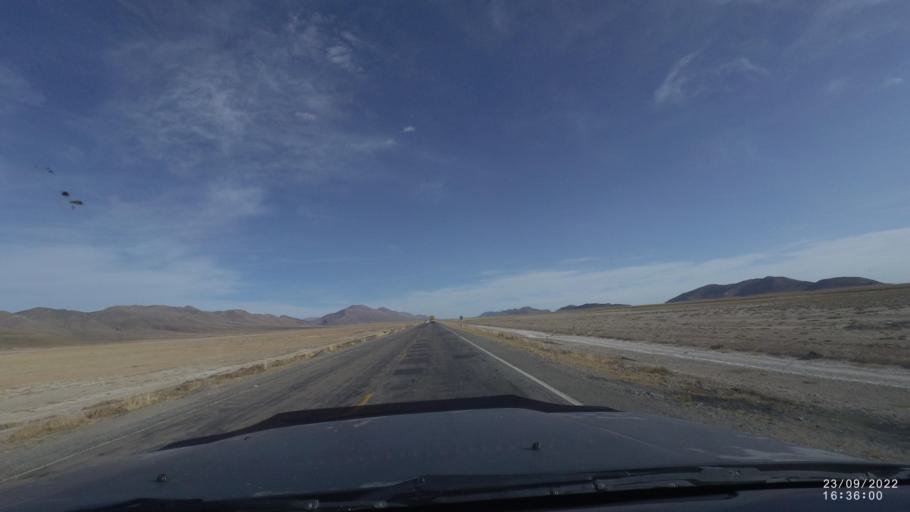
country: BO
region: Oruro
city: Machacamarca
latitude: -18.2131
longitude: -67.0093
